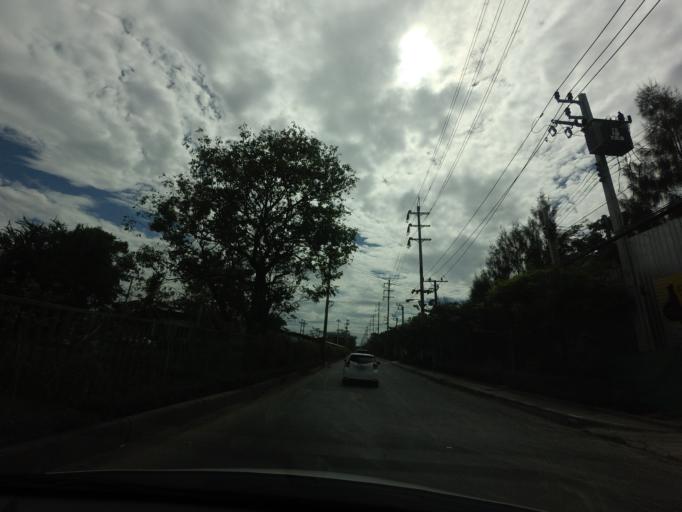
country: TH
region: Bangkok
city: Phra Khanong
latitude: 13.6821
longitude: 100.5914
